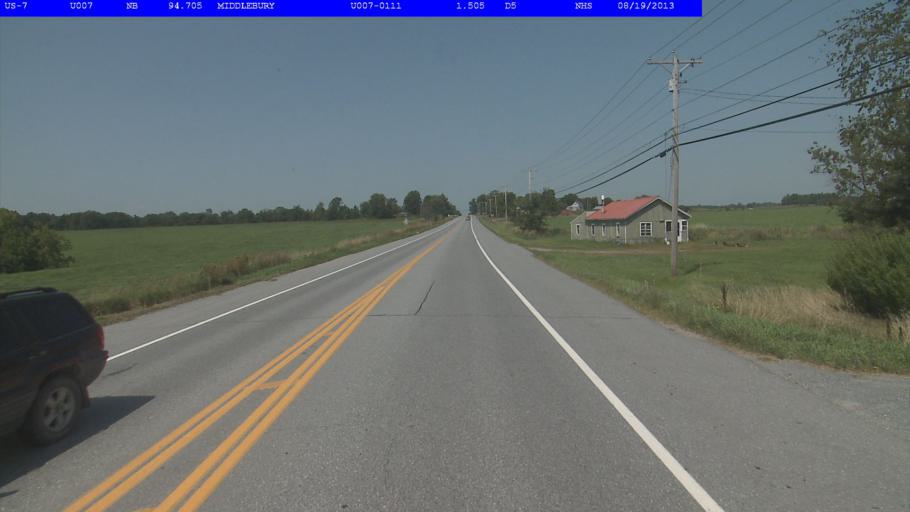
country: US
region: Vermont
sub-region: Addison County
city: Middlebury (village)
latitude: 43.9771
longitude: -73.1193
